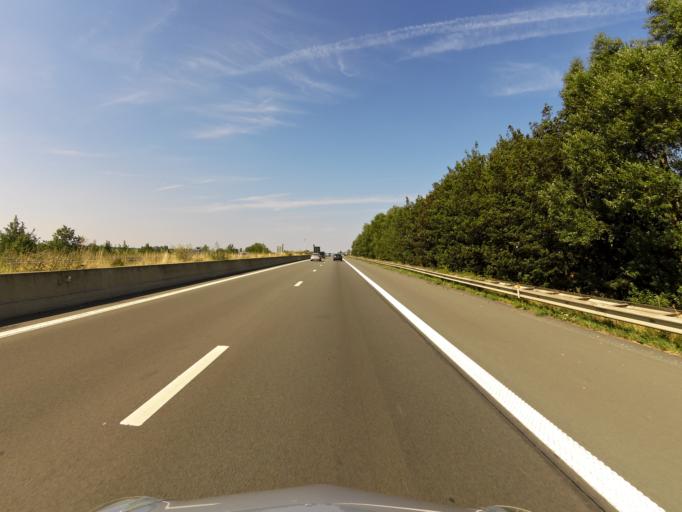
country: BE
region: Flanders
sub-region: Provincie West-Vlaanderen
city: Ardooie
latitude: 50.9899
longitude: 3.1759
